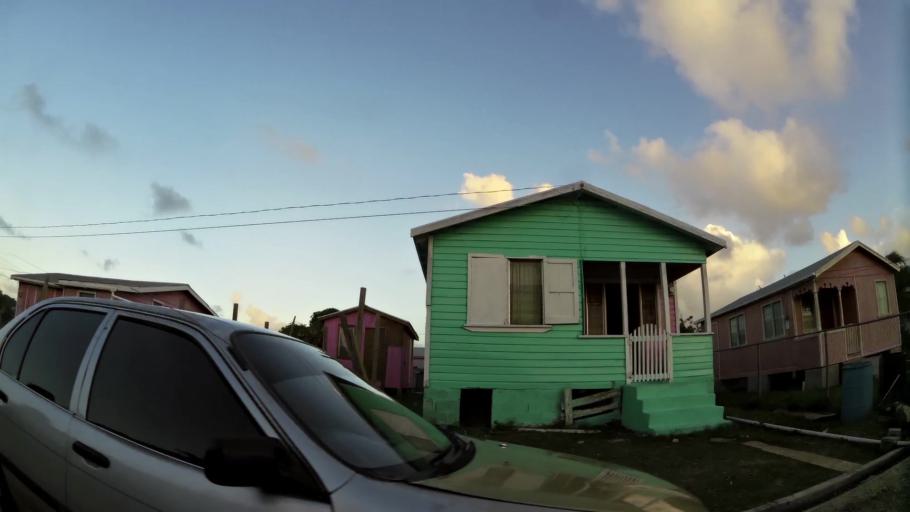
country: AG
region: Saint John
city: Saint John's
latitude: 17.1341
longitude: -61.8404
